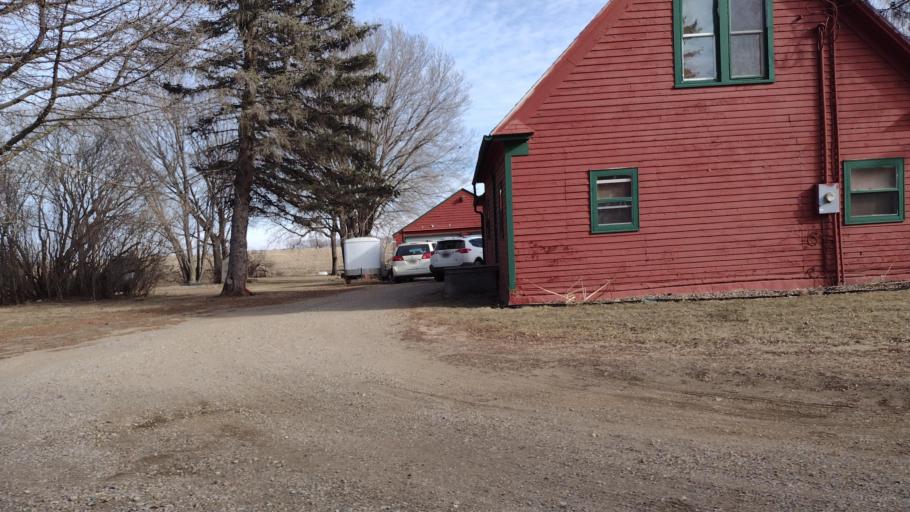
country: US
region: South Dakota
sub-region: Union County
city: Beresford
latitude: 42.9615
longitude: -96.8055
